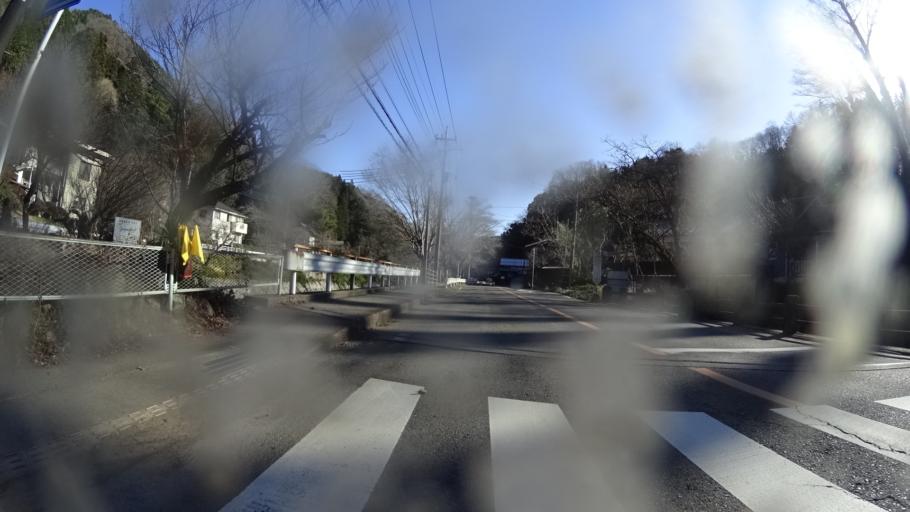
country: JP
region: Yamanashi
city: Uenohara
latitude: 35.6265
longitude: 139.1491
